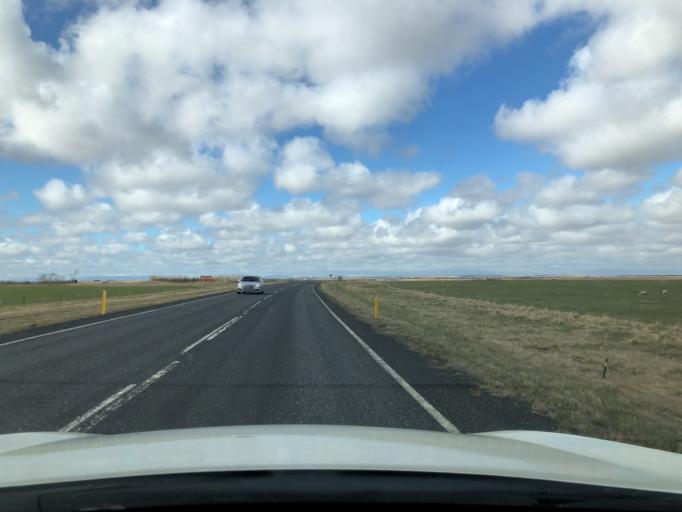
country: IS
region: South
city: Vestmannaeyjar
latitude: 63.7703
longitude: -20.2718
